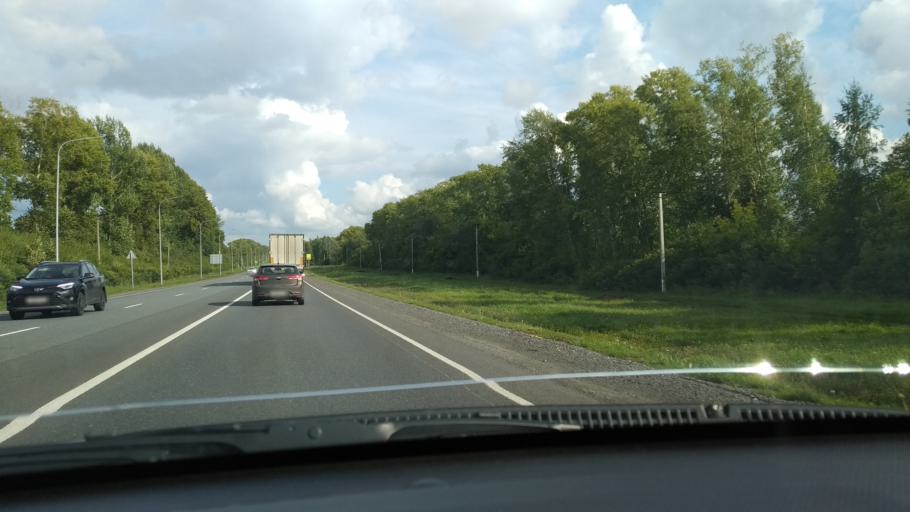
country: RU
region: Tatarstan
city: Stolbishchi
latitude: 55.6545
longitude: 49.3152
